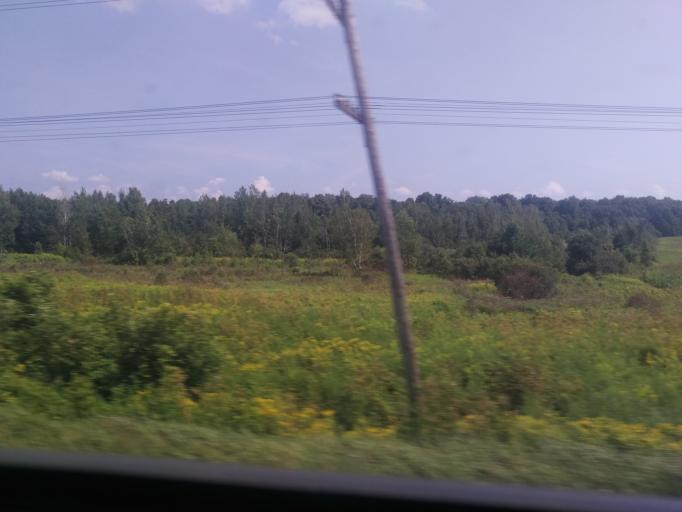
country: CA
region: Ontario
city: Brockville
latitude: 44.5344
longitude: -75.8176
